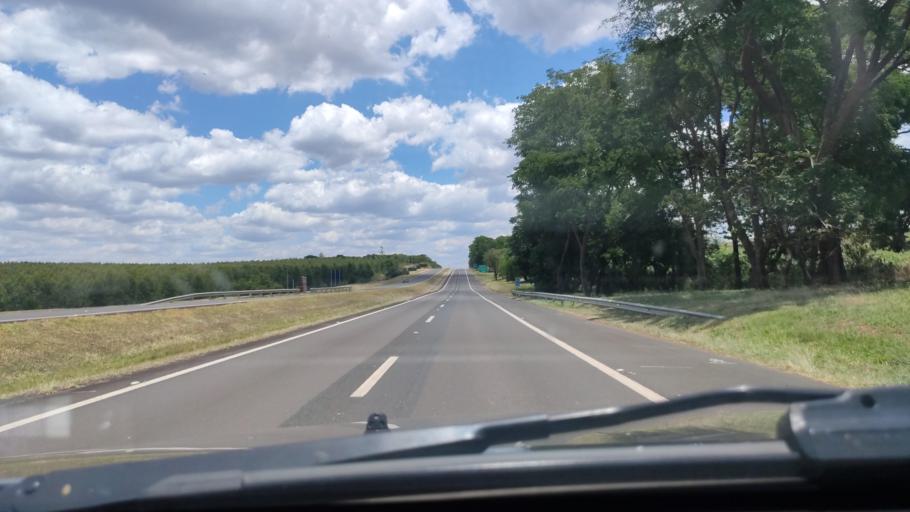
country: BR
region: Sao Paulo
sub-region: Duartina
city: Duartina
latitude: -22.5058
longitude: -49.2886
